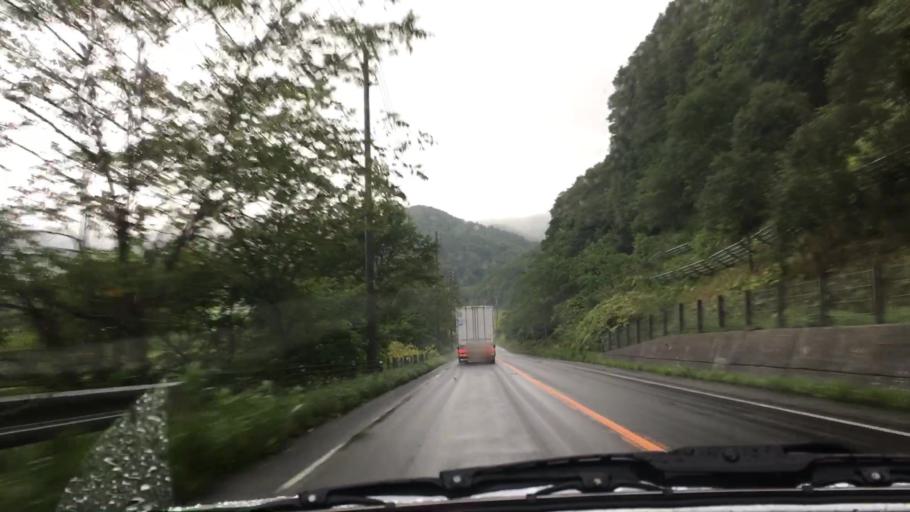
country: JP
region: Hokkaido
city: Niseko Town
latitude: 42.5978
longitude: 140.5884
